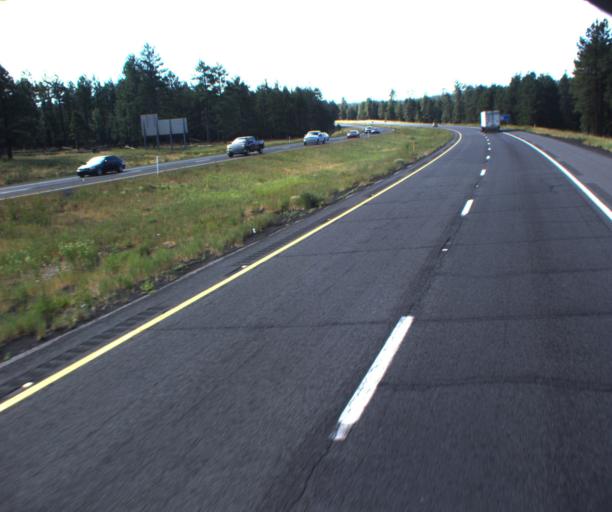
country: US
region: Arizona
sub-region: Coconino County
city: Sedona
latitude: 34.9595
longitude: -111.6793
